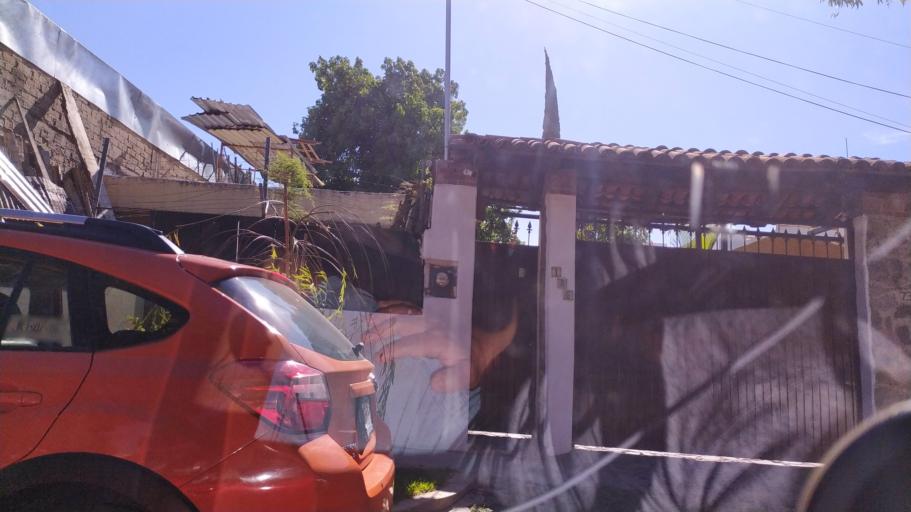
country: MX
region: Jalisco
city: Zapopan2
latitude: 20.6845
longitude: -103.4508
